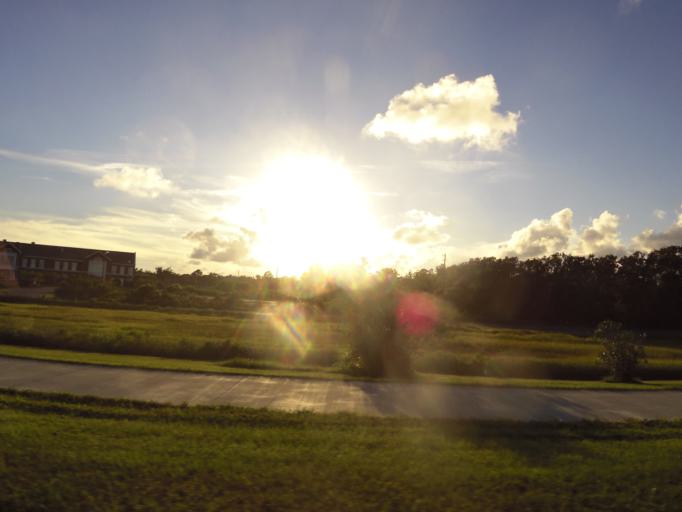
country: US
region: Georgia
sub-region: Glynn County
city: Brunswick
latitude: 31.1408
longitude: -81.4797
